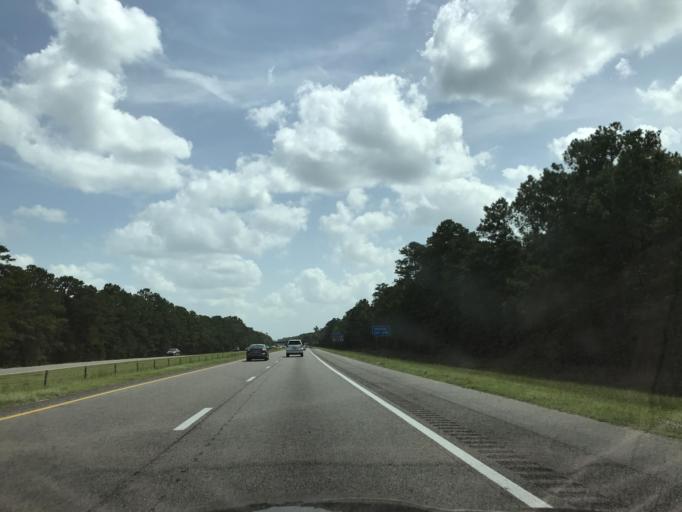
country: US
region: North Carolina
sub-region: Pender County
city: Burgaw
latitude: 34.5855
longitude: -77.9053
